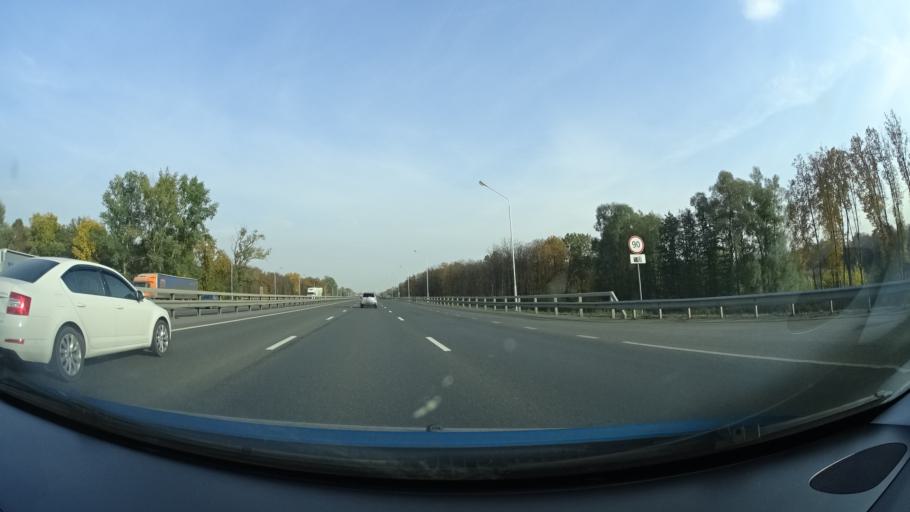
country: RU
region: Bashkortostan
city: Ufa
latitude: 54.6646
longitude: 55.8632
